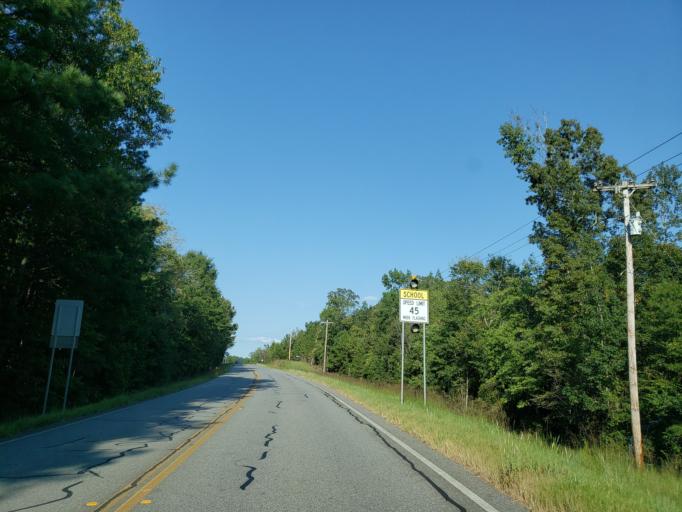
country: US
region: Georgia
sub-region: Whitfield County
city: Varnell
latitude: 34.9093
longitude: -84.8695
